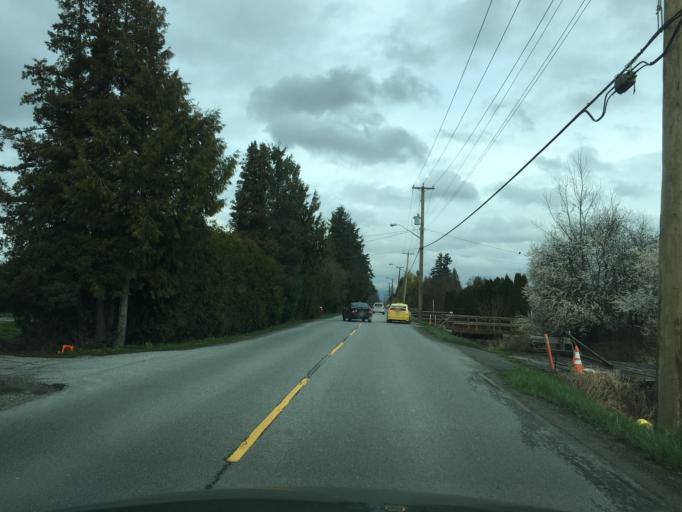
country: CA
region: British Columbia
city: Ladner
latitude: 49.1443
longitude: -123.0694
